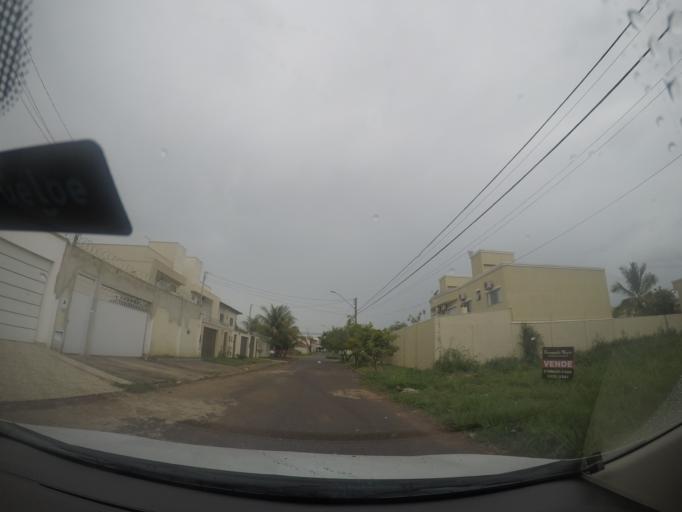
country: BR
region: Goias
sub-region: Goiania
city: Goiania
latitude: -16.6472
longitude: -49.2334
